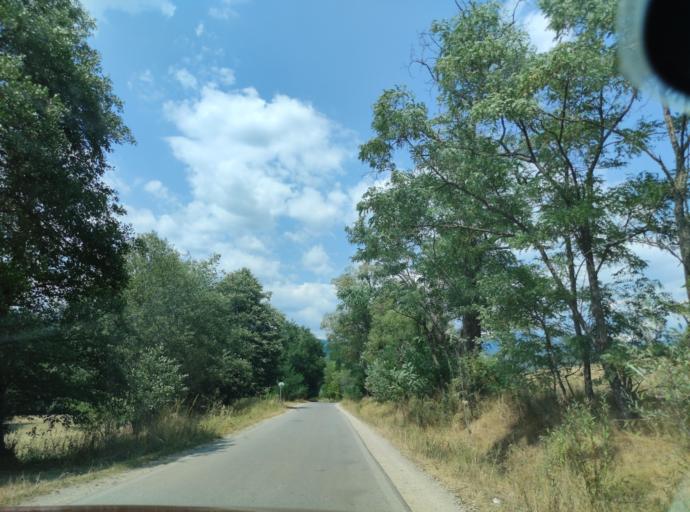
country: BG
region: Blagoevgrad
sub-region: Obshtina Belitsa
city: Belitsa
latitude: 41.9746
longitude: 23.5551
